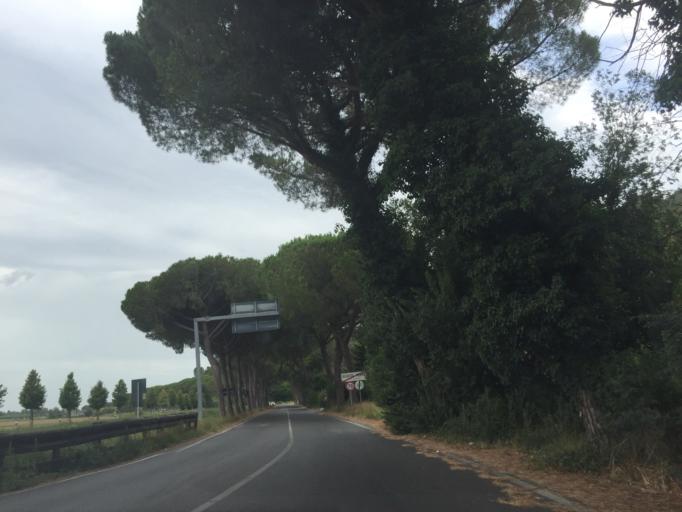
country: IT
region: Tuscany
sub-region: Province of Pisa
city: Uliveto Terme
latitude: 43.7002
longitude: 10.5149
